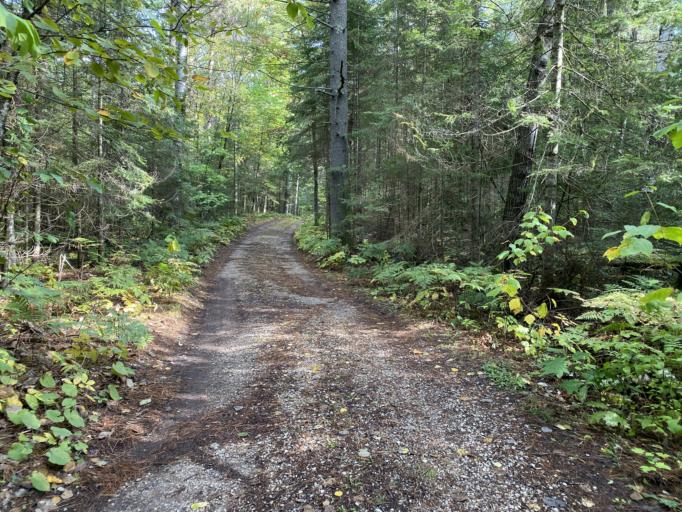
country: US
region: Michigan
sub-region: Mackinac County
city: Saint Ignace
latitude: 45.7491
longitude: -84.8790
